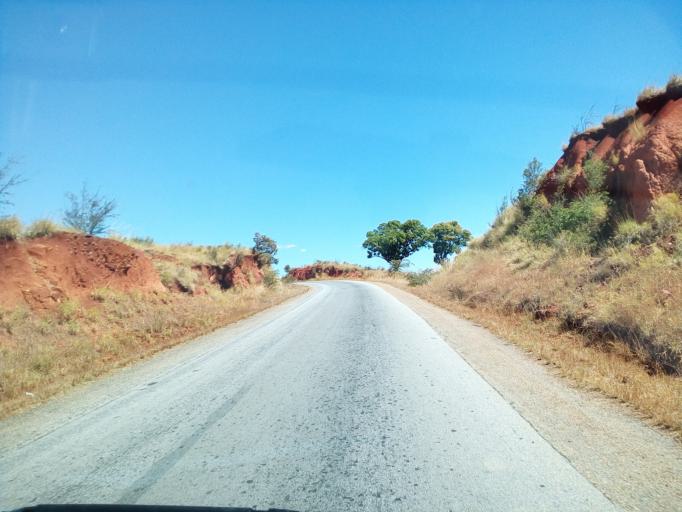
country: MG
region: Betsiboka
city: Maevatanana
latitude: -17.1316
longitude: 46.8092
